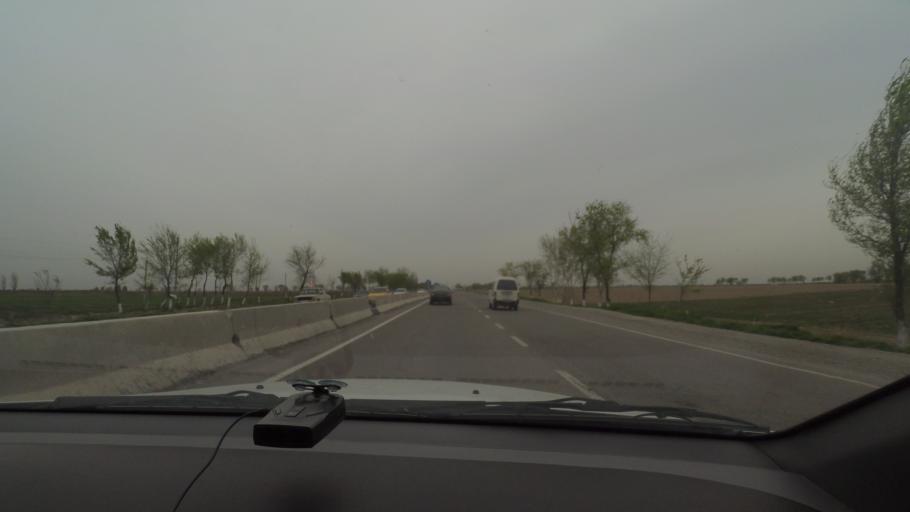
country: KZ
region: Ongtustik Qazaqstan
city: Myrzakent
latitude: 40.5281
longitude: 68.4435
